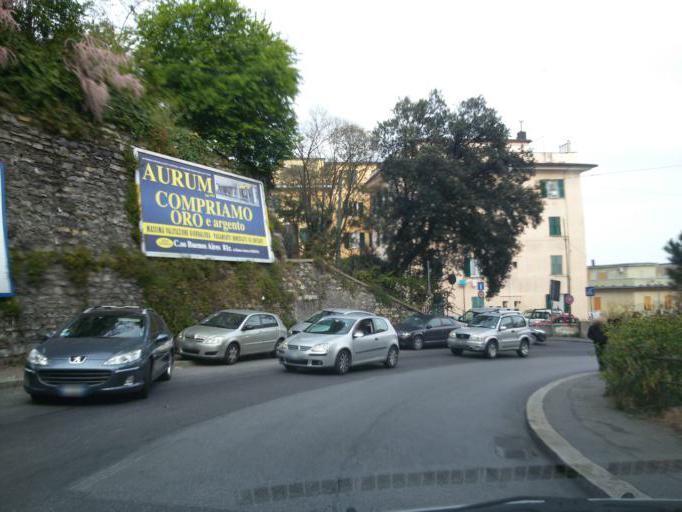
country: IT
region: Liguria
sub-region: Provincia di Genova
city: Genoa
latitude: 44.4113
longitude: 8.9499
